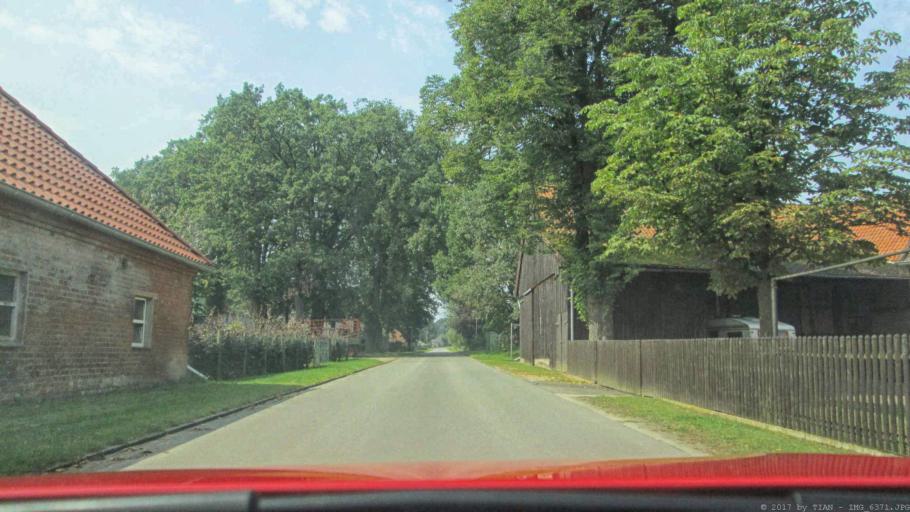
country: DE
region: Lower Saxony
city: Obernholz
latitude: 52.7669
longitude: 10.5968
